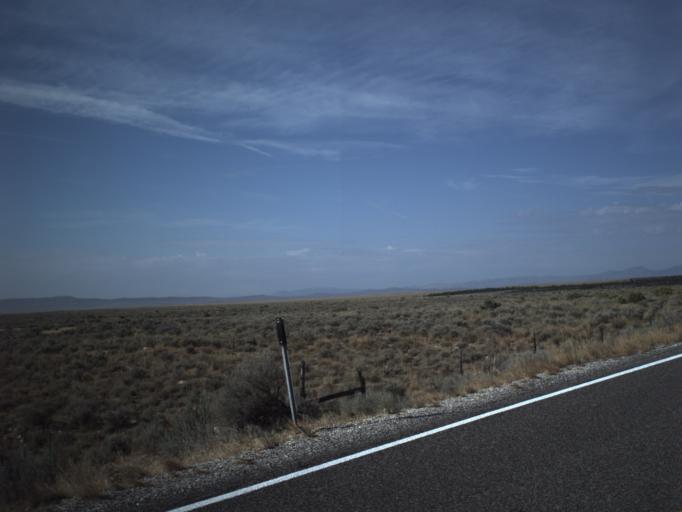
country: US
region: Idaho
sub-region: Cassia County
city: Burley
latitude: 41.8149
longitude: -113.2149
